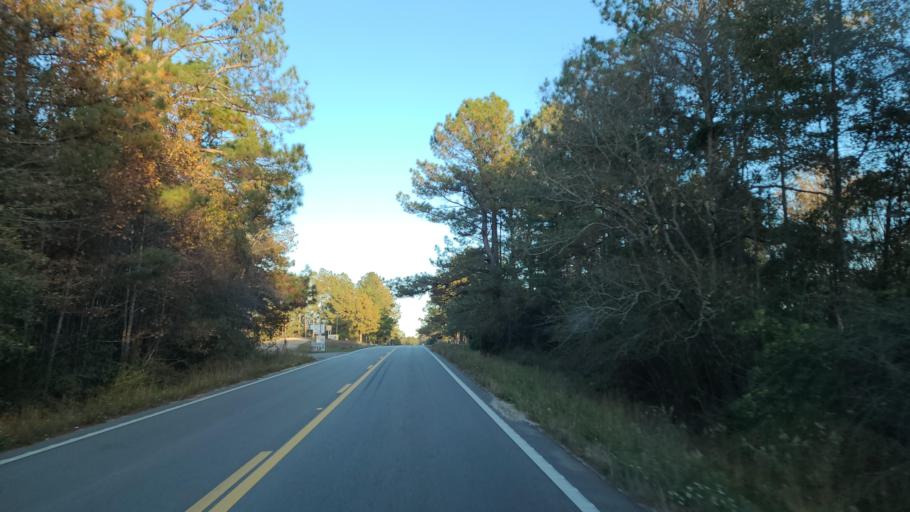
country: US
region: Mississippi
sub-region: Lamar County
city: Lumberton
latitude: 31.0022
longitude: -89.3324
